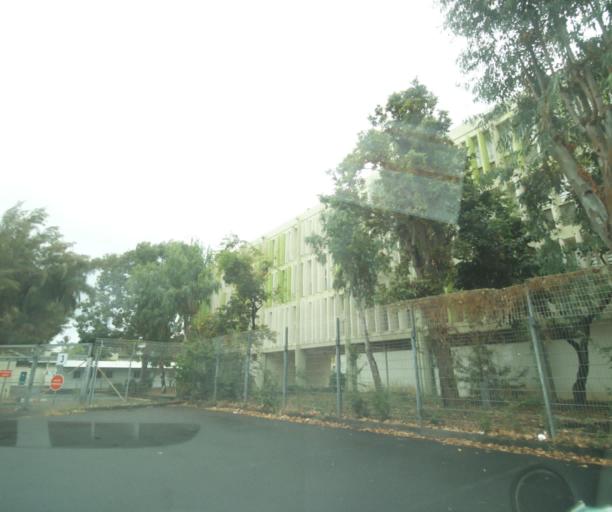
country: RE
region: Reunion
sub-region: Reunion
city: Saint-Paul
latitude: -21.0001
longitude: 55.2804
